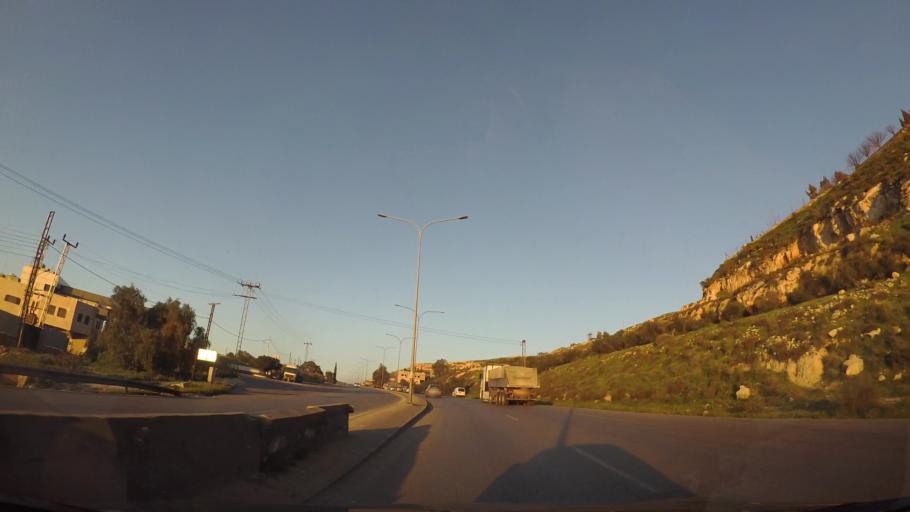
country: JO
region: Amman
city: Umm as Summaq
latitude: 31.8746
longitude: 35.7768
